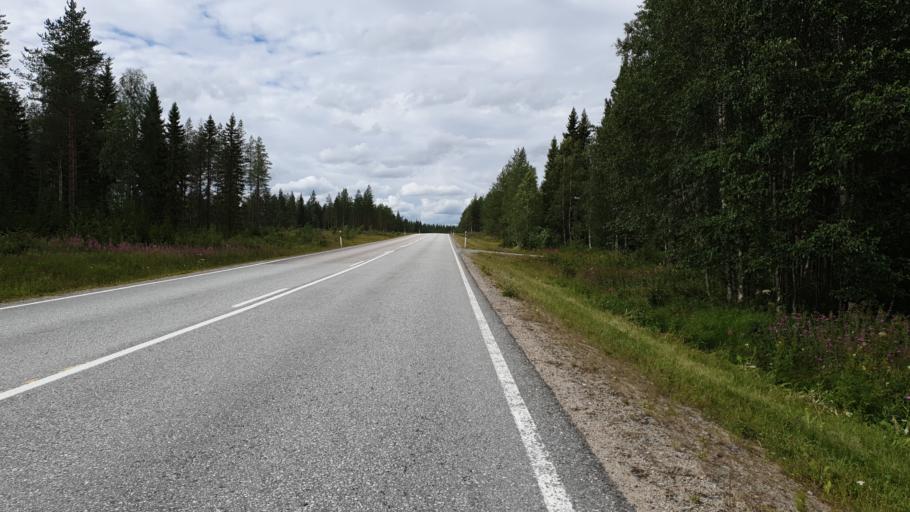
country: FI
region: Kainuu
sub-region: Kehys-Kainuu
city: Kuhmo
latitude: 64.4826
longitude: 29.7797
